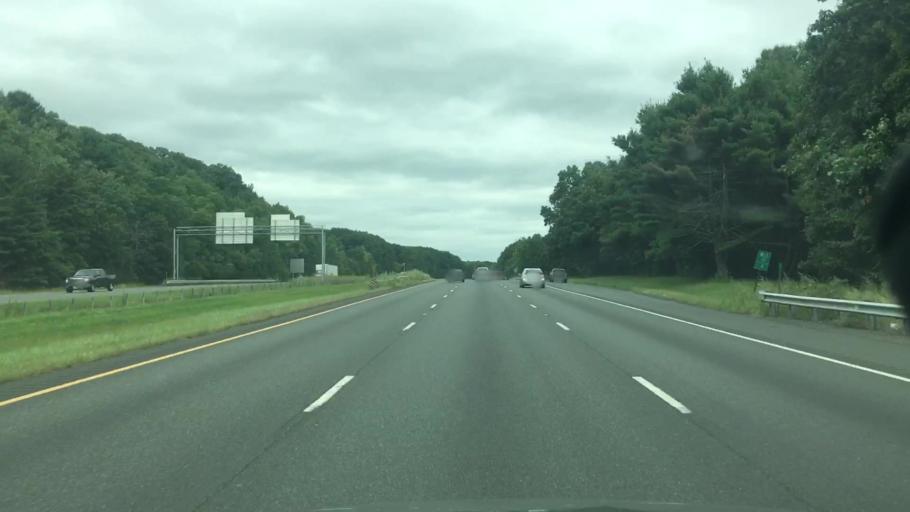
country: US
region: Massachusetts
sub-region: Hampden County
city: Chicopee
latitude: 42.1470
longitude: -72.6426
